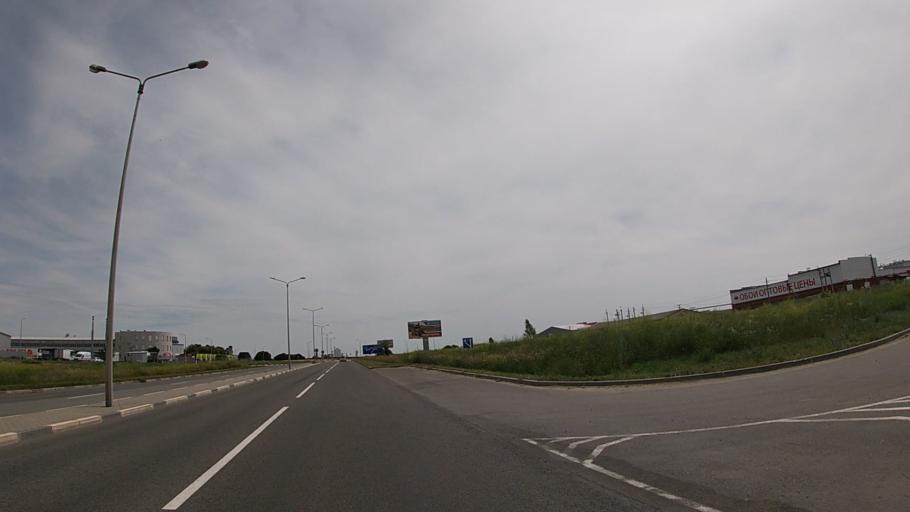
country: RU
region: Belgorod
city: Severnyy
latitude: 50.6601
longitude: 36.5583
